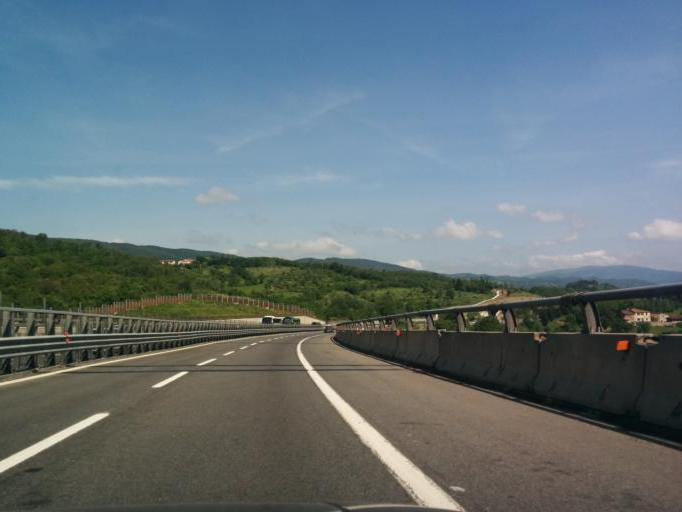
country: IT
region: Tuscany
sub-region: Province of Florence
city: Cavallina
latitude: 43.9548
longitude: 11.2105
